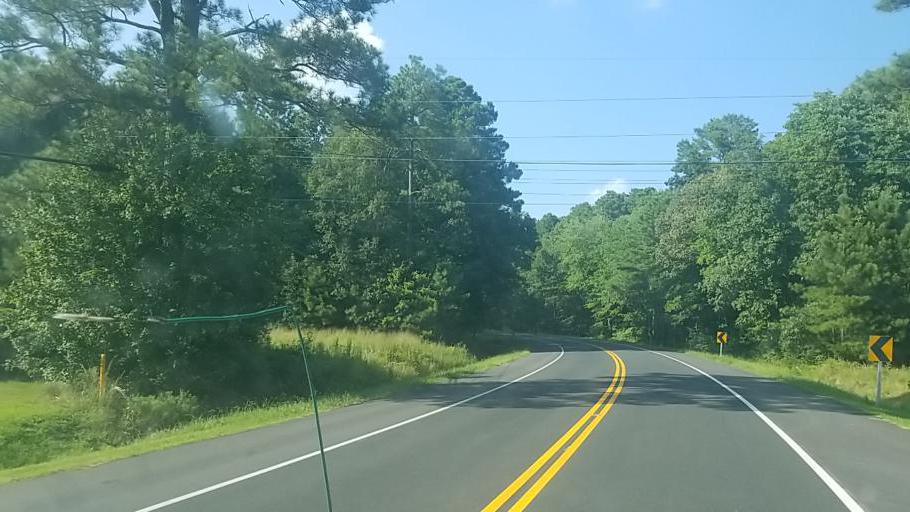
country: US
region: Maryland
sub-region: Worcester County
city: Ocean Pines
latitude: 38.3703
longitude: -75.1984
